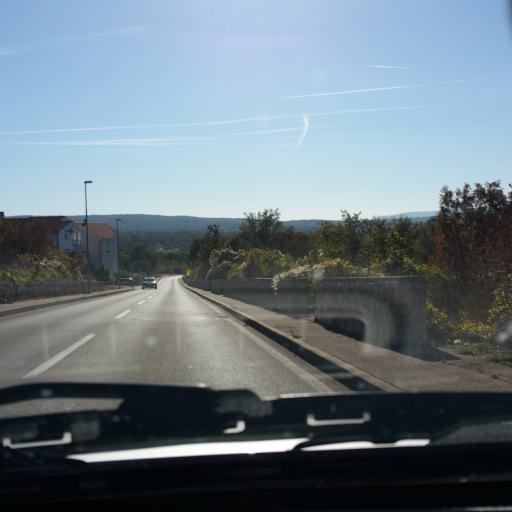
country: HR
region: Primorsko-Goranska
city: Njivice
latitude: 45.1293
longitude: 14.5396
